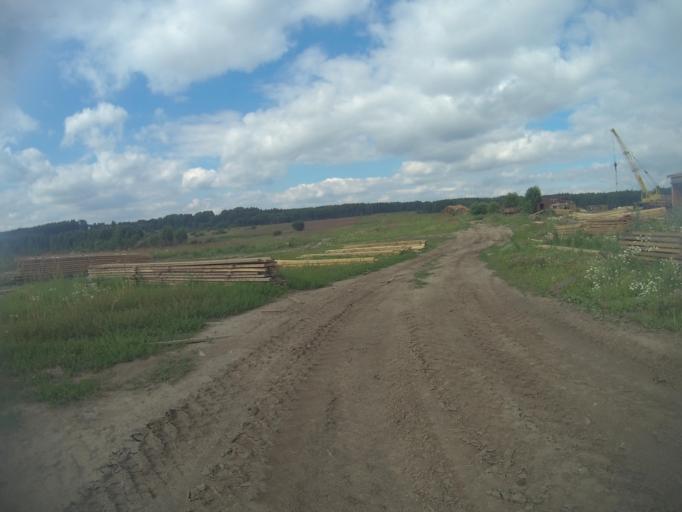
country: RU
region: Vladimir
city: Vorsha
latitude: 56.0056
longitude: 40.1822
